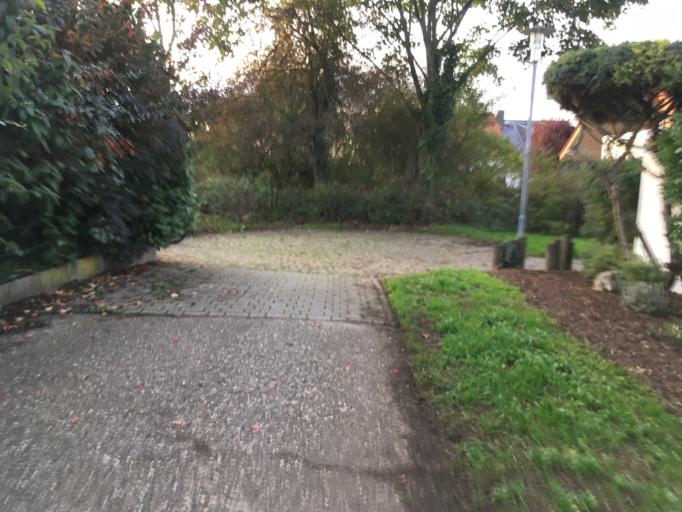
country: DE
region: Baden-Wuerttemberg
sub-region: Karlsruhe Region
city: Nussloch
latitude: 49.3233
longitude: 8.6878
